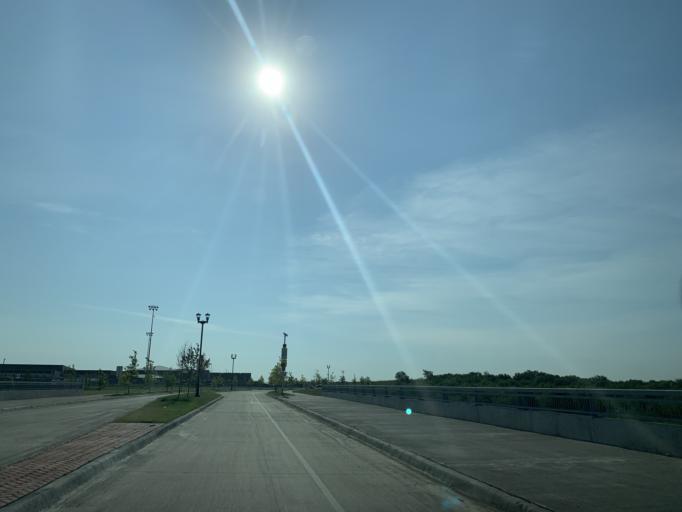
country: US
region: Texas
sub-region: Tarrant County
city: Blue Mound
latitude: 32.8898
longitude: -97.3154
